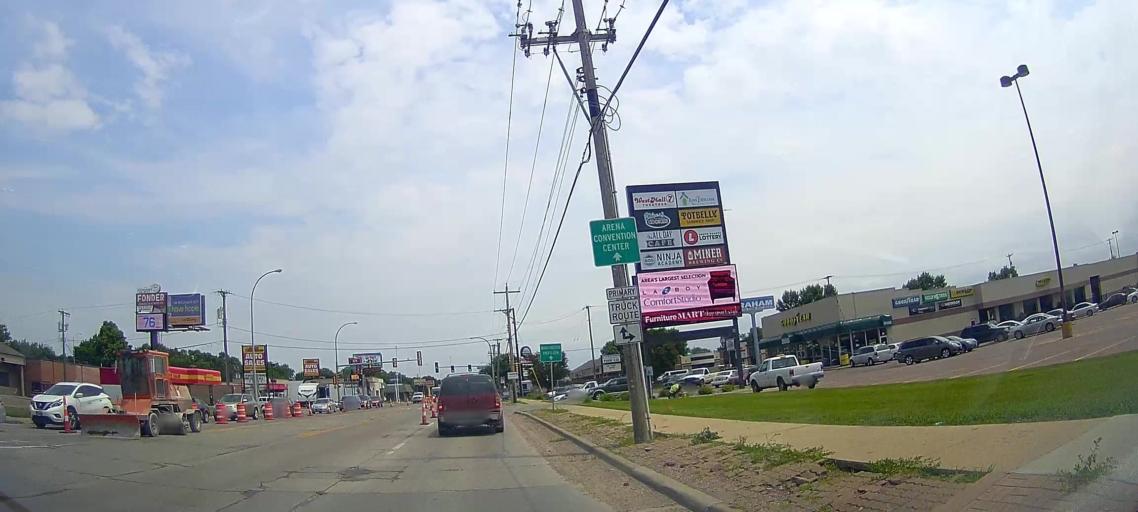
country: US
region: South Dakota
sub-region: Minnehaha County
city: Sioux Falls
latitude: 43.5148
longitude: -96.7524
